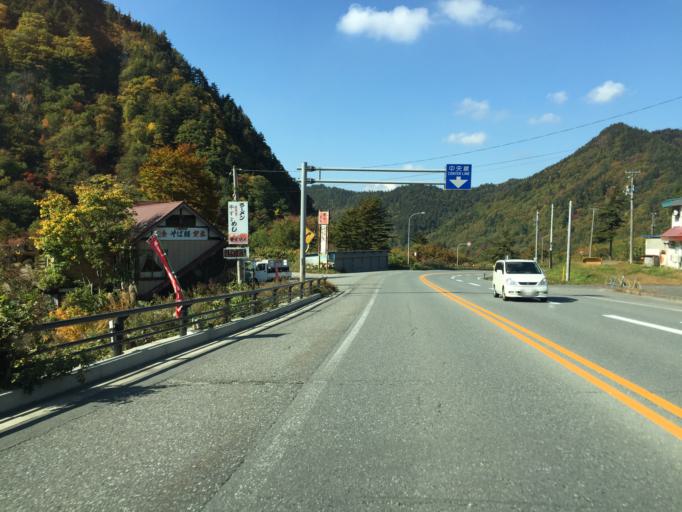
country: JP
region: Yamagata
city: Yonezawa
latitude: 37.8635
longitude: 140.2314
